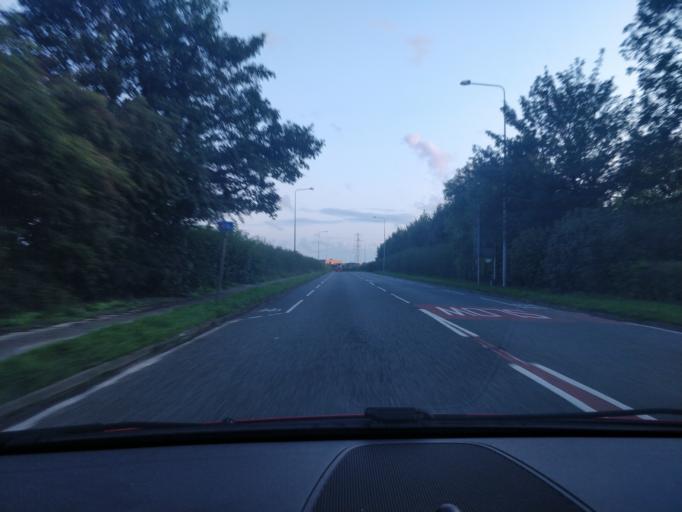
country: GB
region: England
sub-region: Lancashire
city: Tarleton
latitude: 53.6940
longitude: -2.8131
